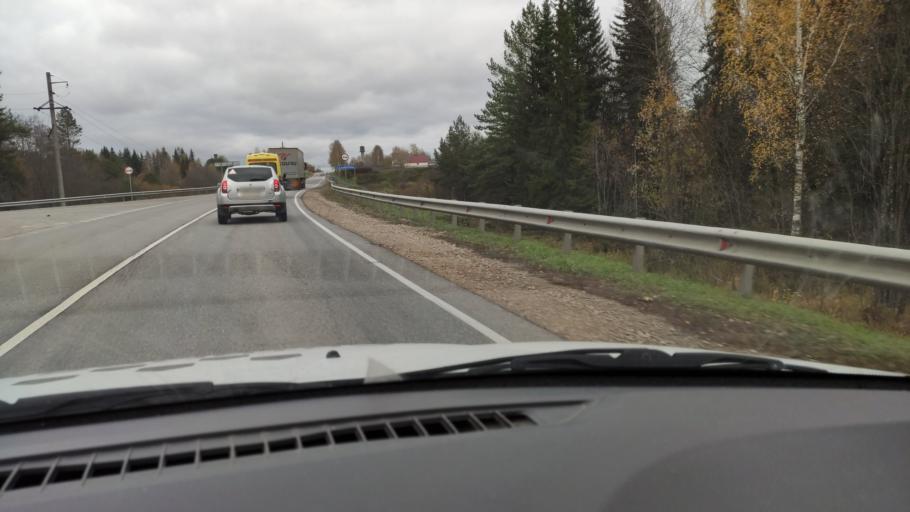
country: RU
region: Kirov
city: Slobodskoy
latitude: 58.7819
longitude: 50.4160
